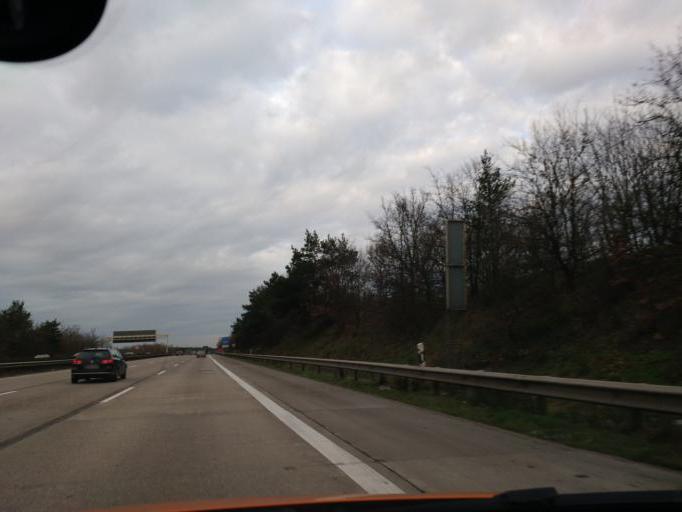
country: DE
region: Lower Saxony
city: Essel
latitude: 52.6834
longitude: 9.6902
